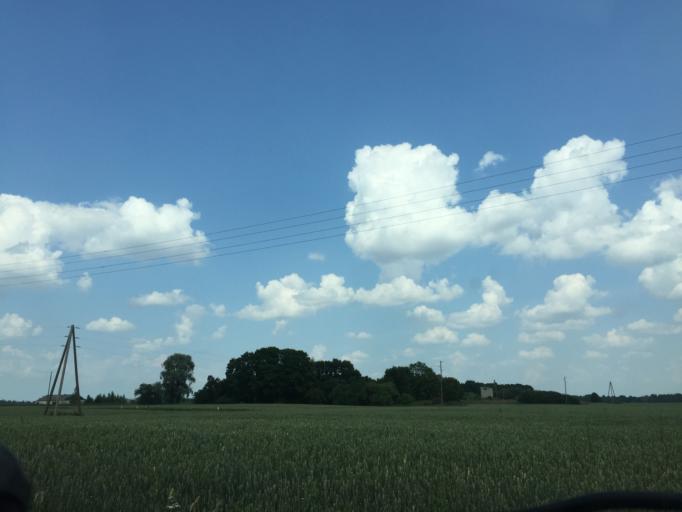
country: LT
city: Zagare
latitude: 56.3407
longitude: 23.1508
